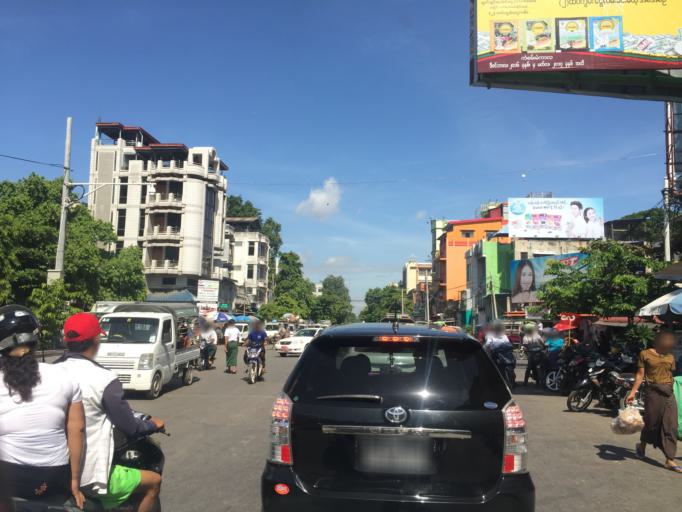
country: MM
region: Mandalay
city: Mandalay
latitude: 21.9836
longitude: 96.0766
